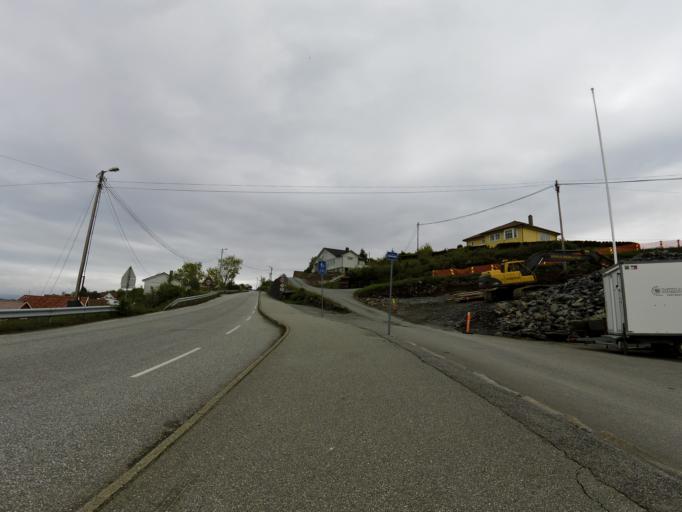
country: NO
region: Hordaland
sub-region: Sveio
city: Sveio
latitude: 59.6017
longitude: 5.2112
